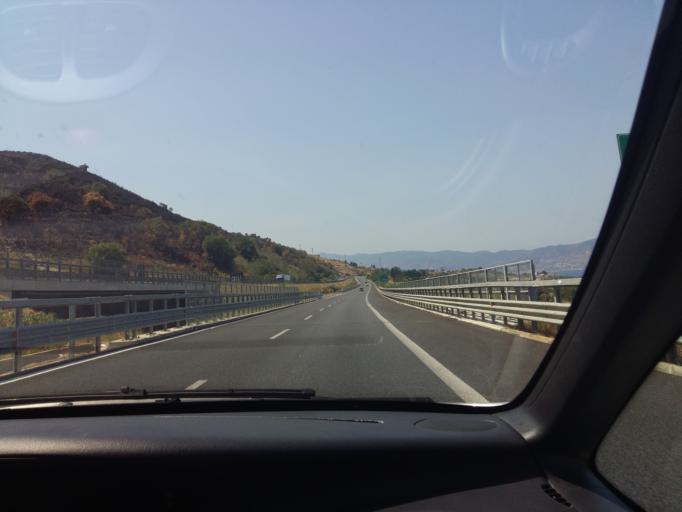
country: IT
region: Calabria
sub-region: Provincia di Reggio Calabria
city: Villa San Giovanni
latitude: 38.2320
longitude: 15.6651
